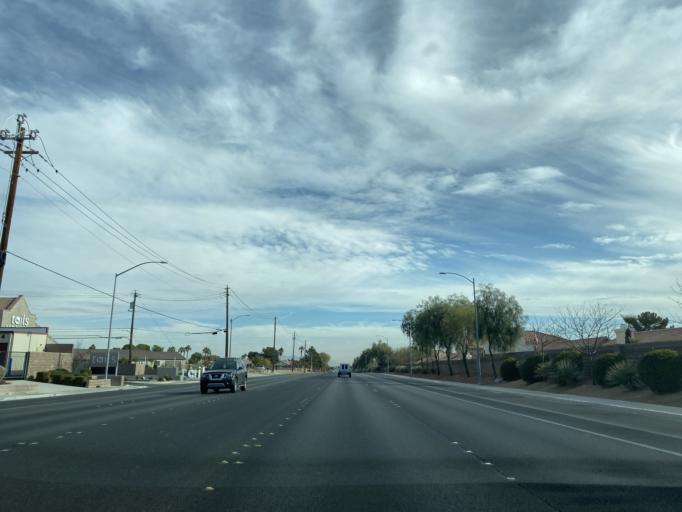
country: US
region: Nevada
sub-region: Clark County
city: Las Vegas
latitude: 36.2464
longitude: -115.2244
